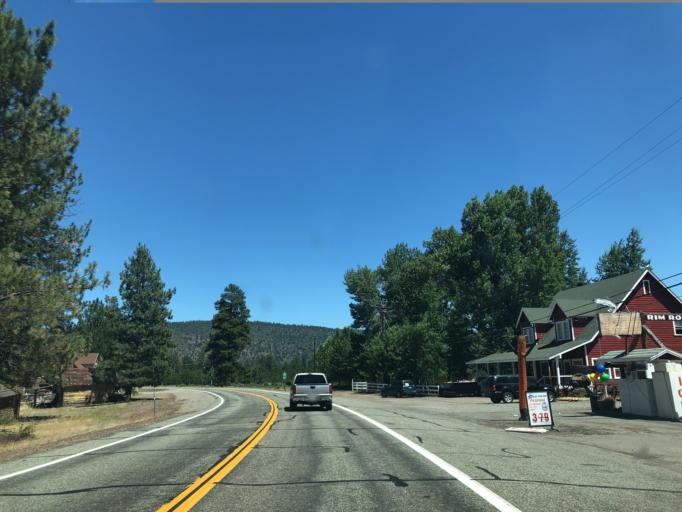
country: US
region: California
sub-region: Shasta County
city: Burney
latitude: 40.6748
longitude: -121.4336
